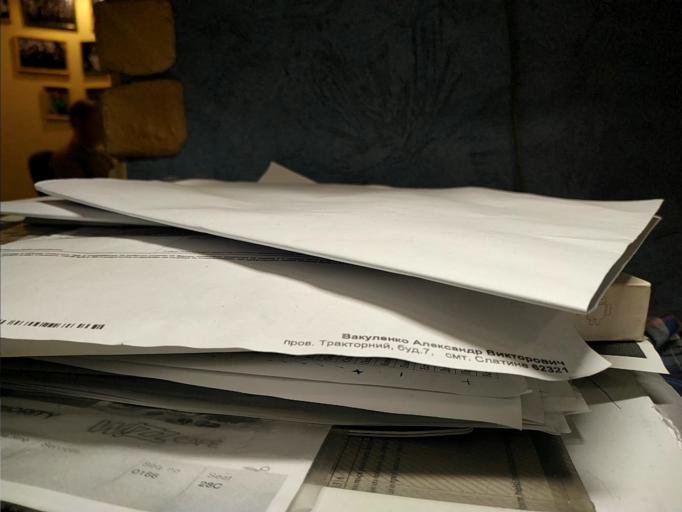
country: RU
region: Tverskaya
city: Zubtsov
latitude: 56.1348
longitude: 34.4895
